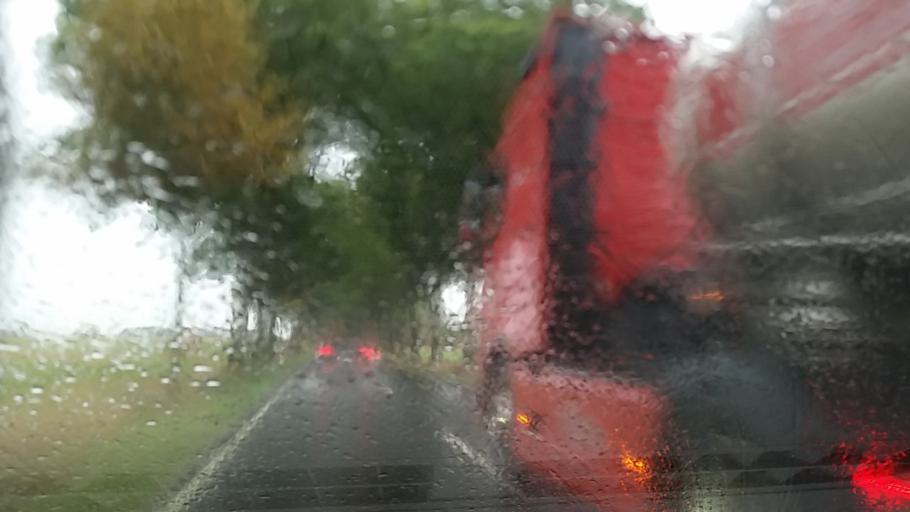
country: DE
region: Lower Saxony
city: Tulau
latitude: 52.6530
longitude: 10.8111
